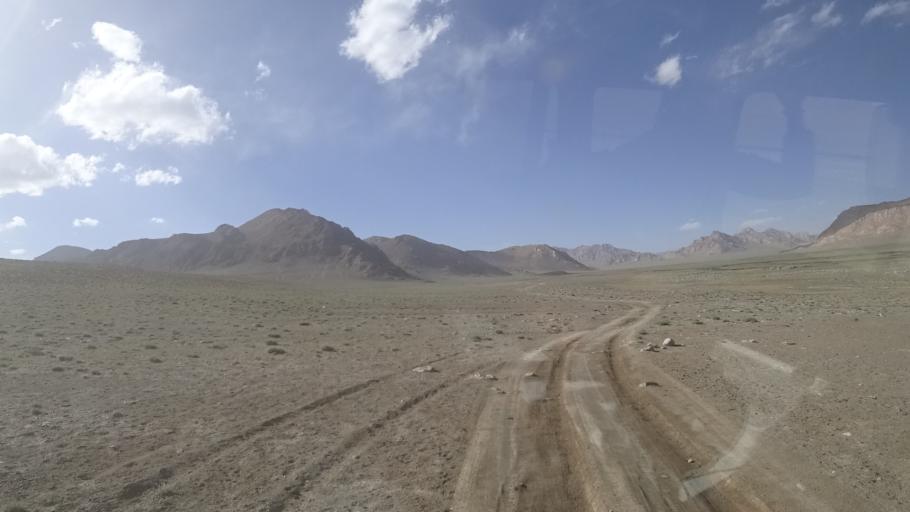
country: TJ
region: Gorno-Badakhshan
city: Murghob
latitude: 37.5848
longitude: 74.1542
